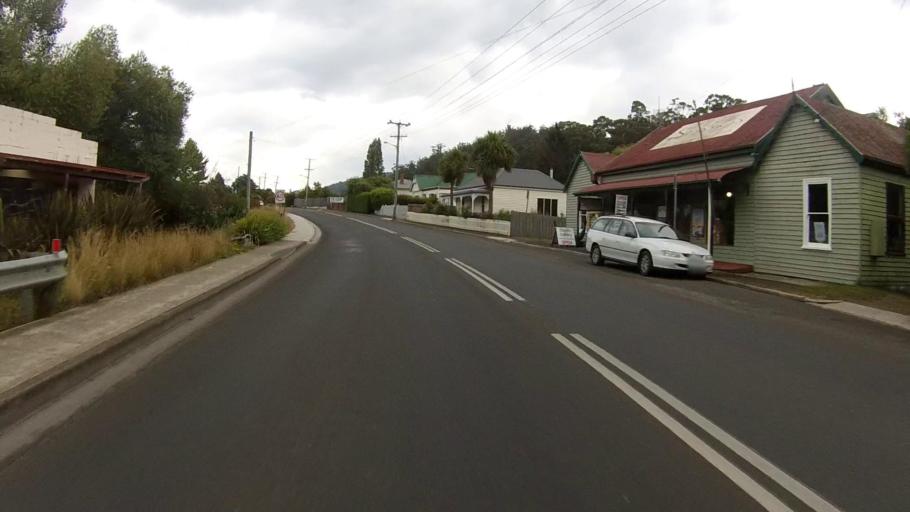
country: AU
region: Tasmania
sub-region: Huon Valley
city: Cygnet
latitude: -43.1551
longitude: 147.0738
